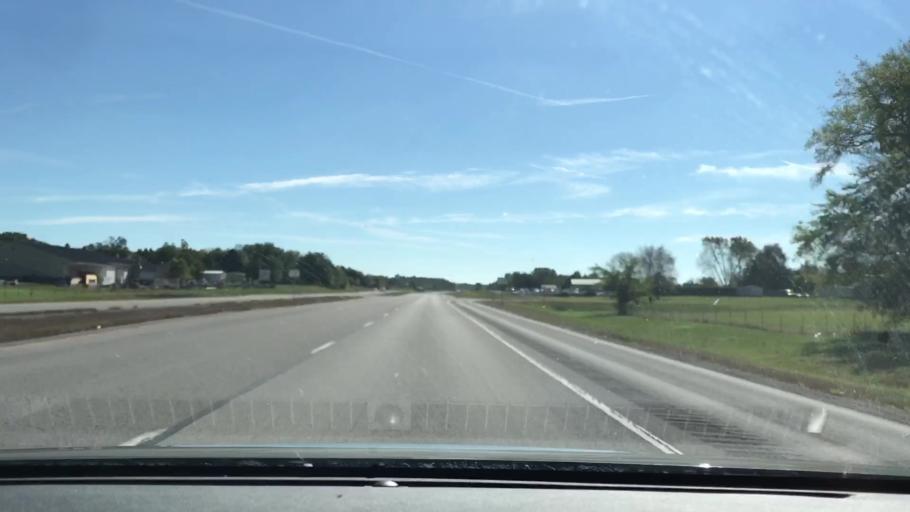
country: US
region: Kentucky
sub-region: Todd County
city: Elkton
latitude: 36.8371
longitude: -87.2395
